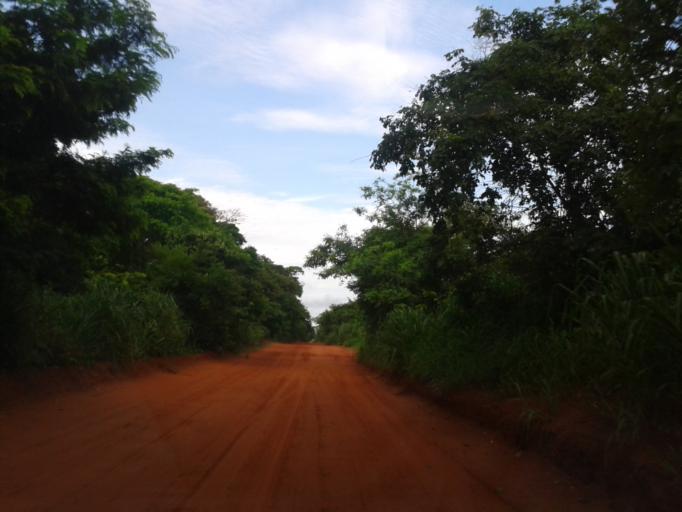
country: BR
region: Minas Gerais
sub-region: Santa Vitoria
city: Santa Vitoria
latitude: -19.1180
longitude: -50.5324
